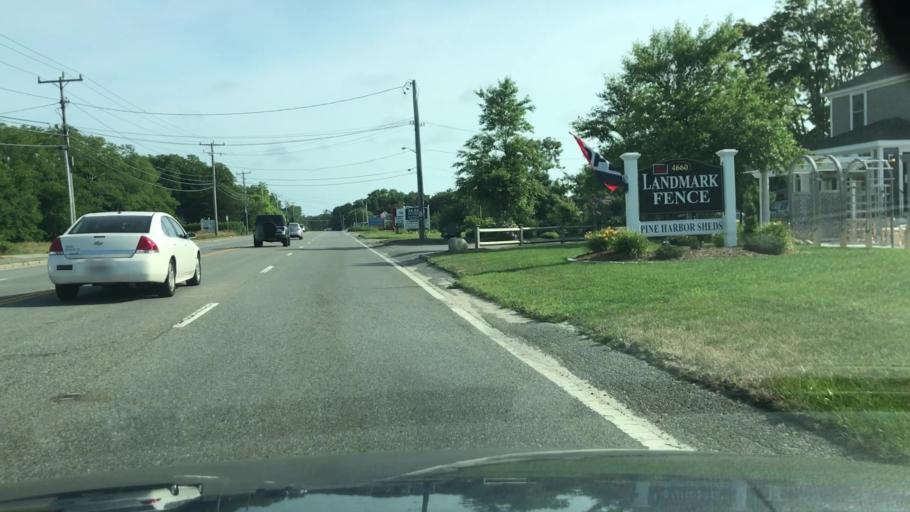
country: US
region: Massachusetts
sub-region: Barnstable County
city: North Eastham
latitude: 41.8582
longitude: -69.9865
